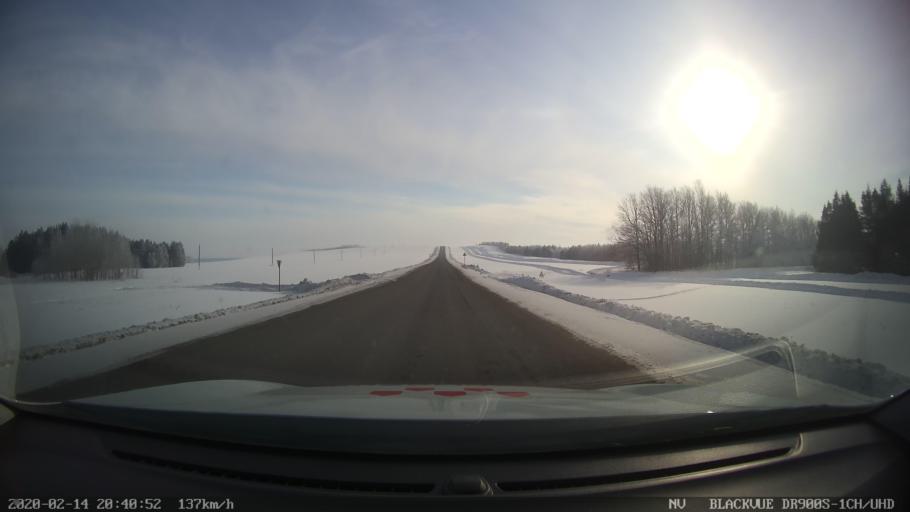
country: RU
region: Tatarstan
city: Kuybyshevskiy Zaton
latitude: 55.3360
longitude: 49.1030
